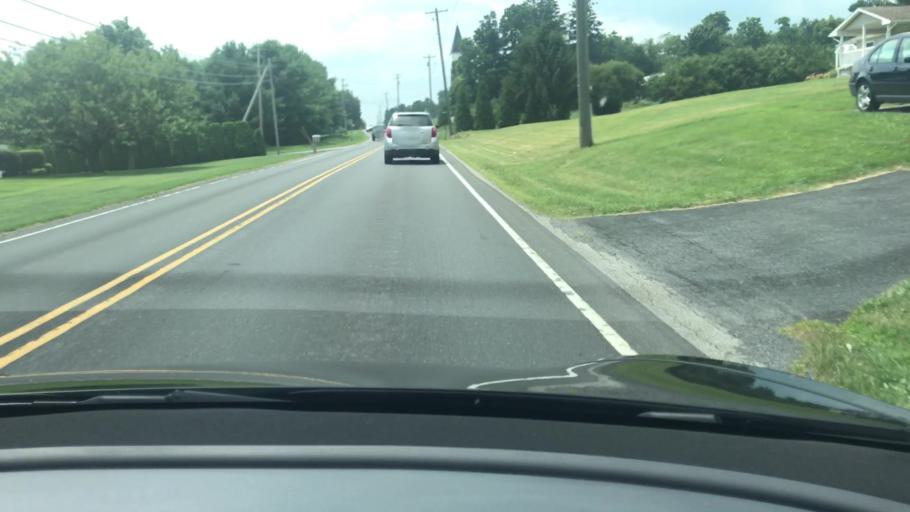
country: US
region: Pennsylvania
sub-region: Centre County
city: Stormstown
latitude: 40.8205
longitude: -77.9742
